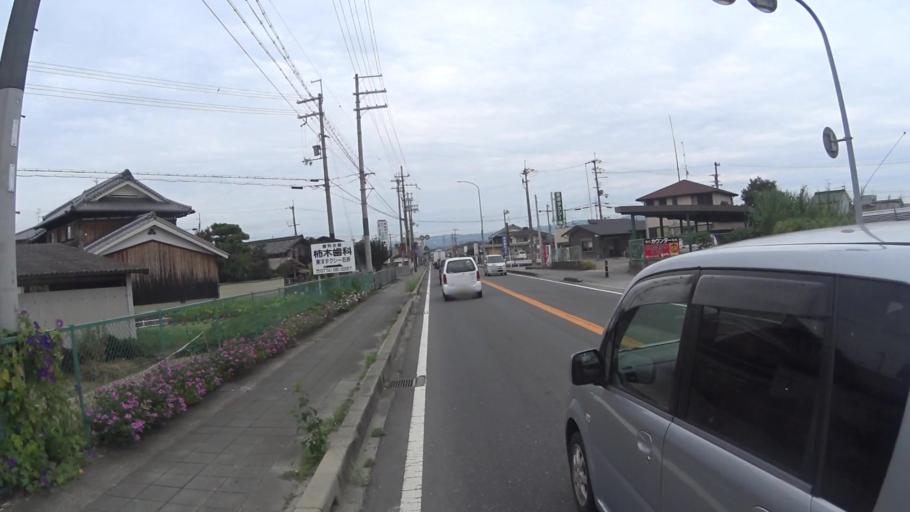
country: JP
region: Nara
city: Nara-shi
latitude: 34.7511
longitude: 135.8160
